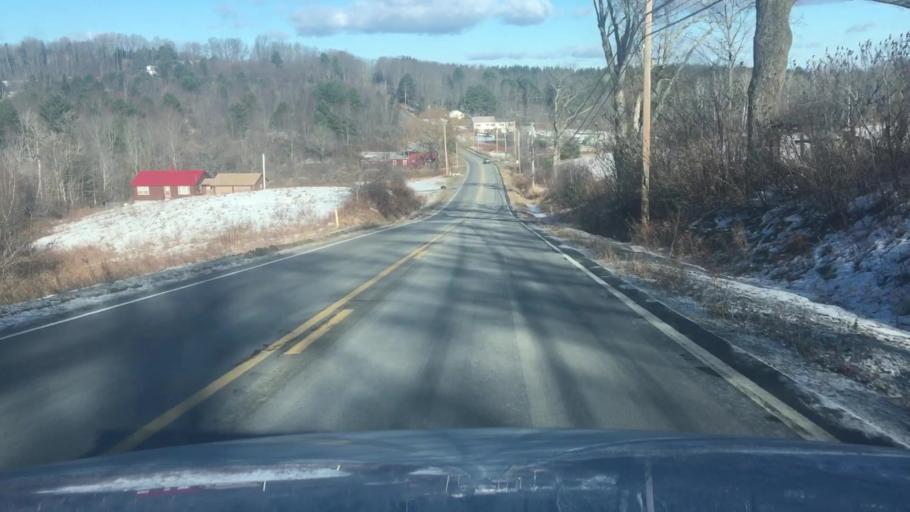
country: US
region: Maine
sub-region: Somerset County
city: Fairfield
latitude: 44.6475
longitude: -69.6762
